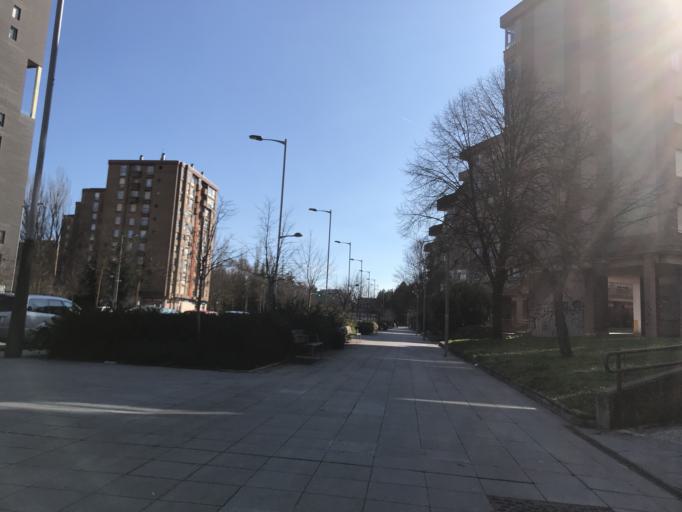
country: ES
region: Basque Country
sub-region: Provincia de Alava
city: Gasteiz / Vitoria
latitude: 42.8542
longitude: -2.6577
